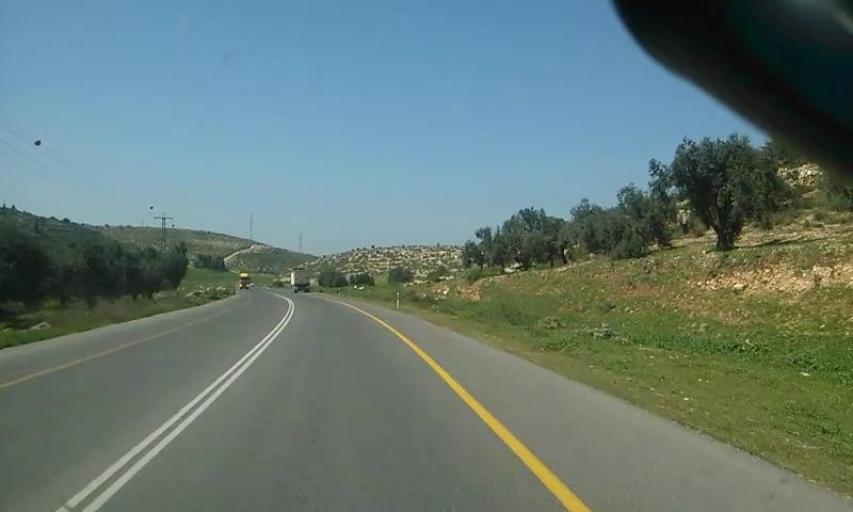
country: PS
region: West Bank
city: Idhna
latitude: 31.5795
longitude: 34.9773
